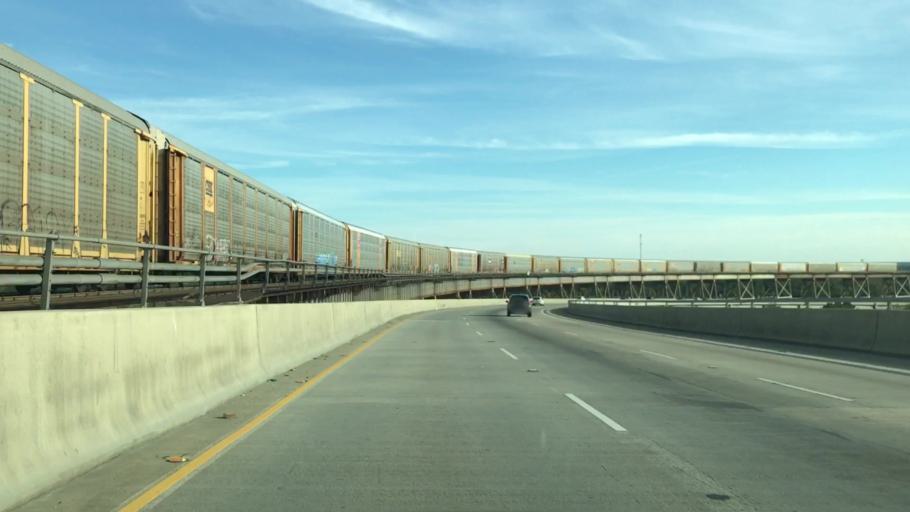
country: US
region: Louisiana
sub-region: Jefferson Parish
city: Bridge City
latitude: 29.9406
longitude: -90.1650
